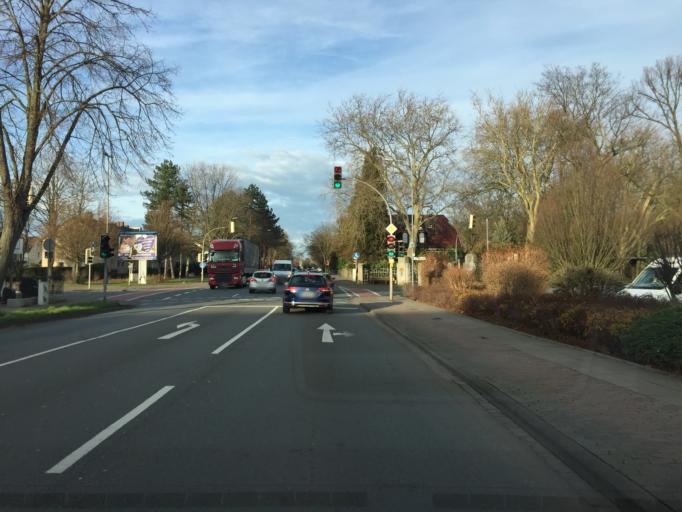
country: DE
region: North Rhine-Westphalia
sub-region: Regierungsbezirk Detmold
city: Minden
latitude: 52.3080
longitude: 8.9153
